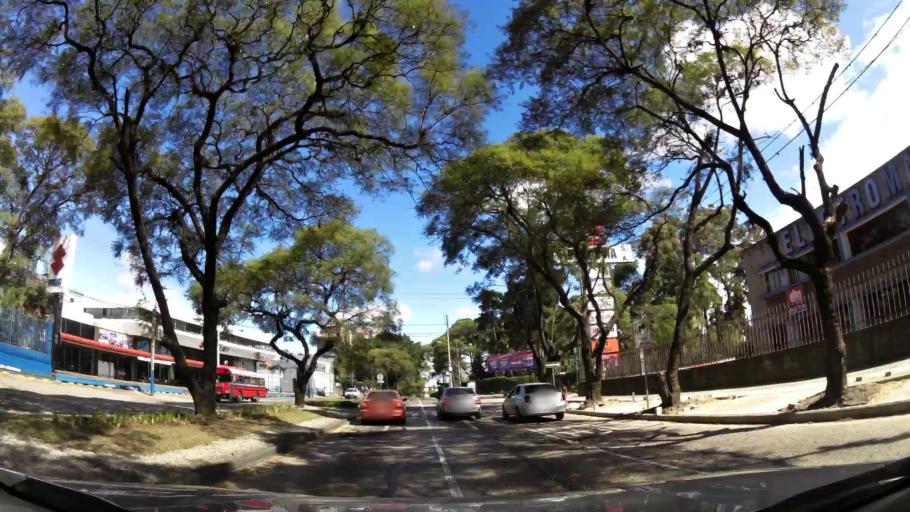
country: GT
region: Guatemala
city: Guatemala City
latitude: 14.6078
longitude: -90.5266
